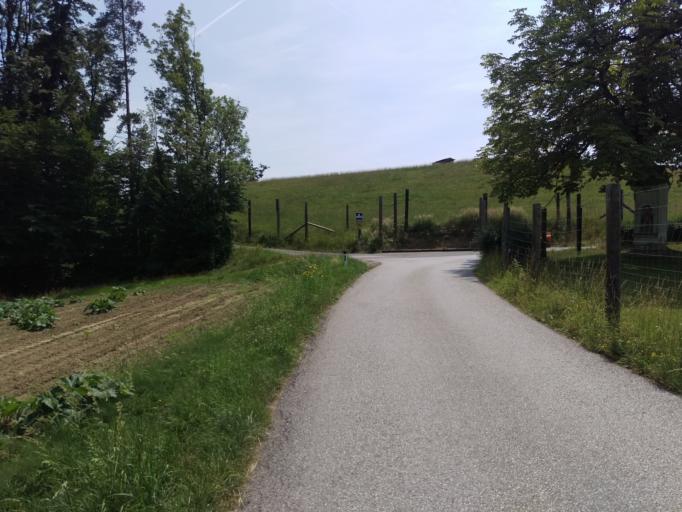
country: AT
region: Styria
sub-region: Graz Stadt
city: Mariatrost
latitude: 47.1097
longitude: 15.4844
